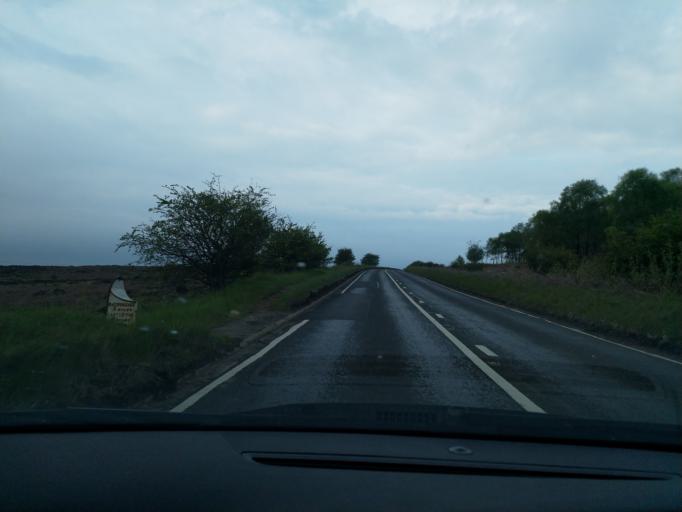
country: GB
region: England
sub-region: Derbyshire
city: Hathersage
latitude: 53.3190
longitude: -1.6176
